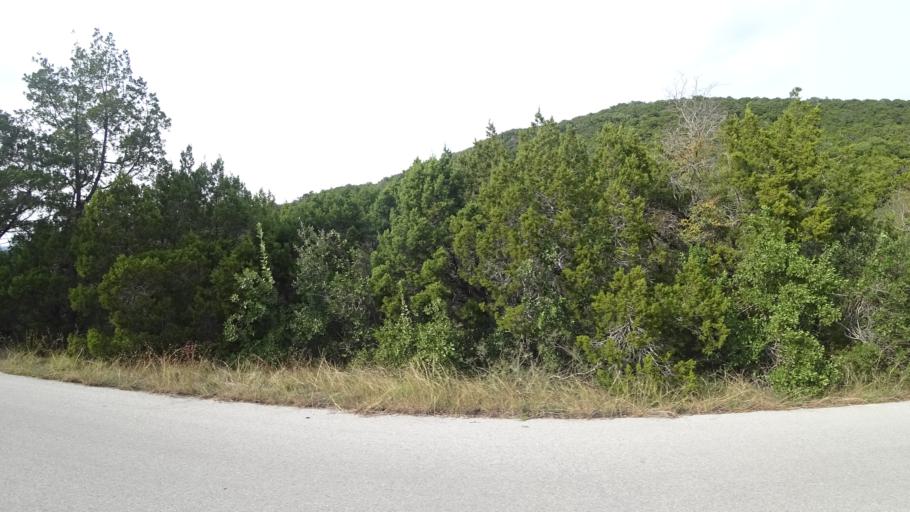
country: US
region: Texas
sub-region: Travis County
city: Hudson Bend
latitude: 30.3960
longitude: -97.8742
